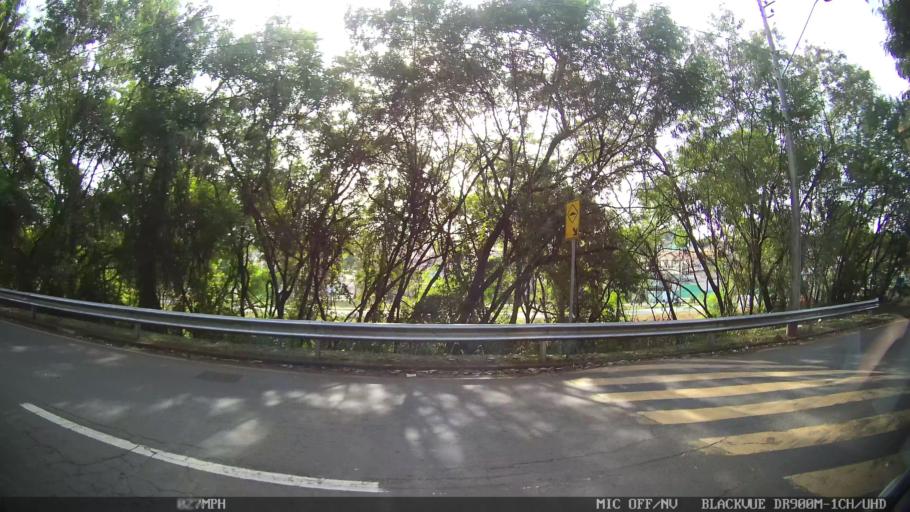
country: BR
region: Sao Paulo
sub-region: Piracicaba
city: Piracicaba
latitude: -22.7347
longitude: -47.6696
